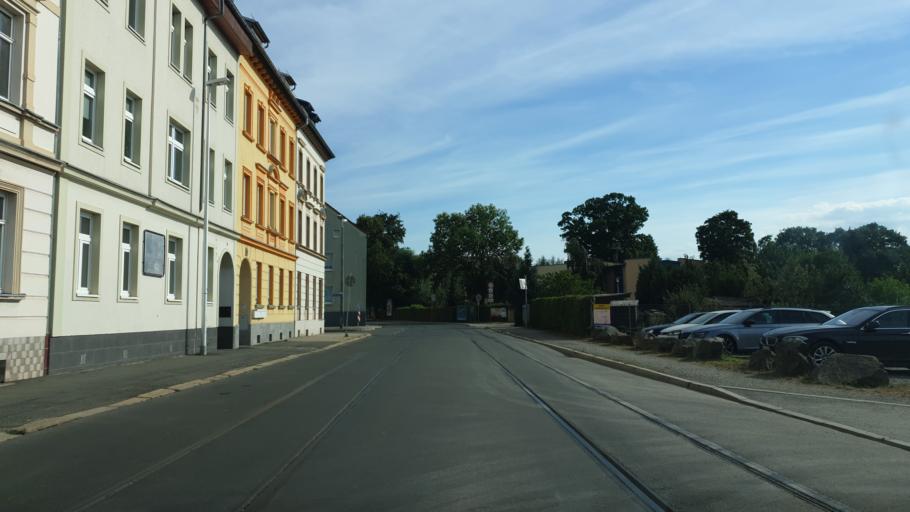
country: DE
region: Thuringia
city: Gera
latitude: 50.8550
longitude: 12.0808
